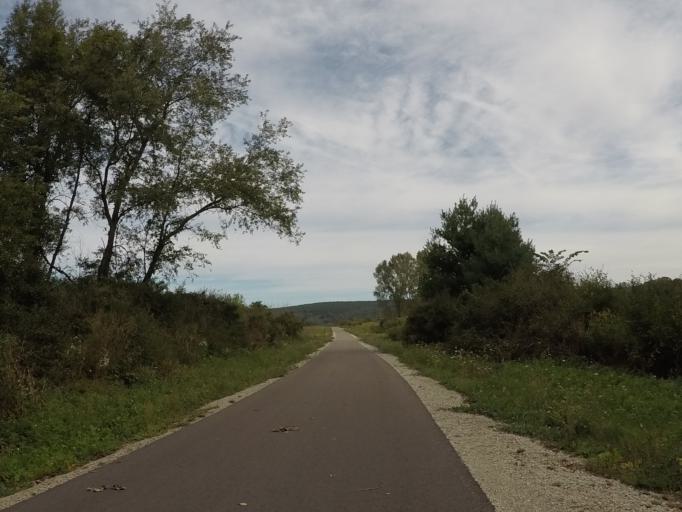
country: US
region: Wisconsin
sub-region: Sauk County
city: Prairie du Sac
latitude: 43.3611
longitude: -89.7400
